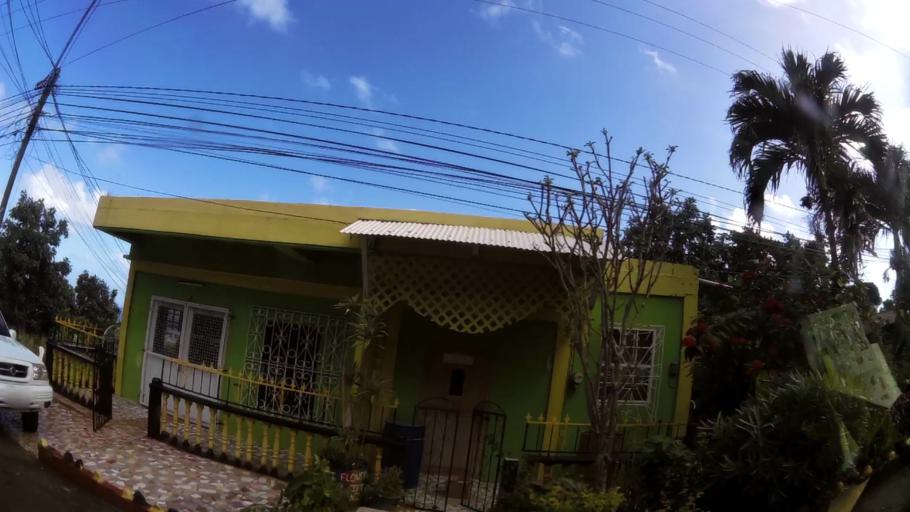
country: DM
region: Saint Andrew
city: Marigot
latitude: 15.5371
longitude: -61.2790
